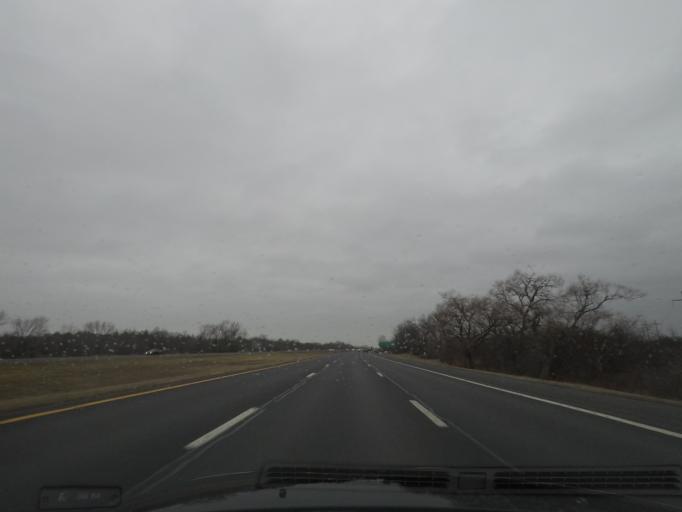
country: US
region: New York
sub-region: Rensselaer County
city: Hampton Manor
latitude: 42.6366
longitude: -73.7075
